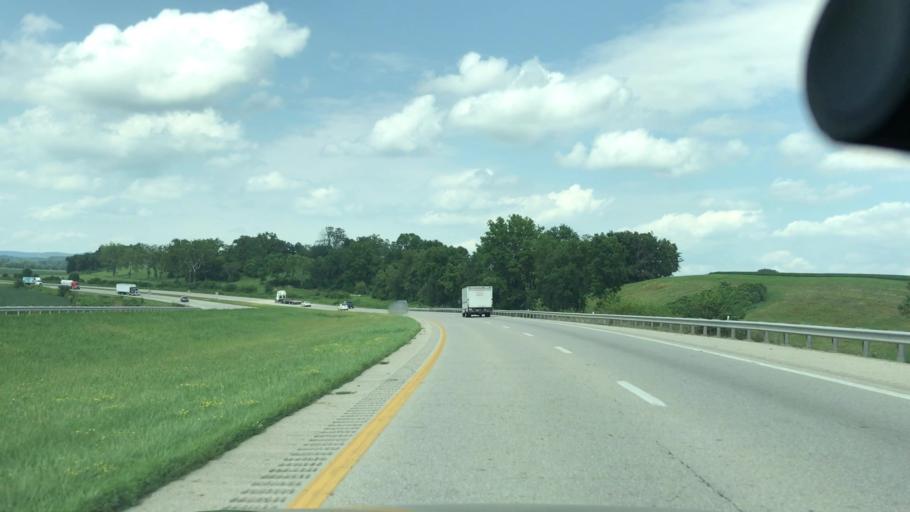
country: US
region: Ohio
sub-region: Ross County
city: Chillicothe
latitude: 39.2779
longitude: -82.8837
